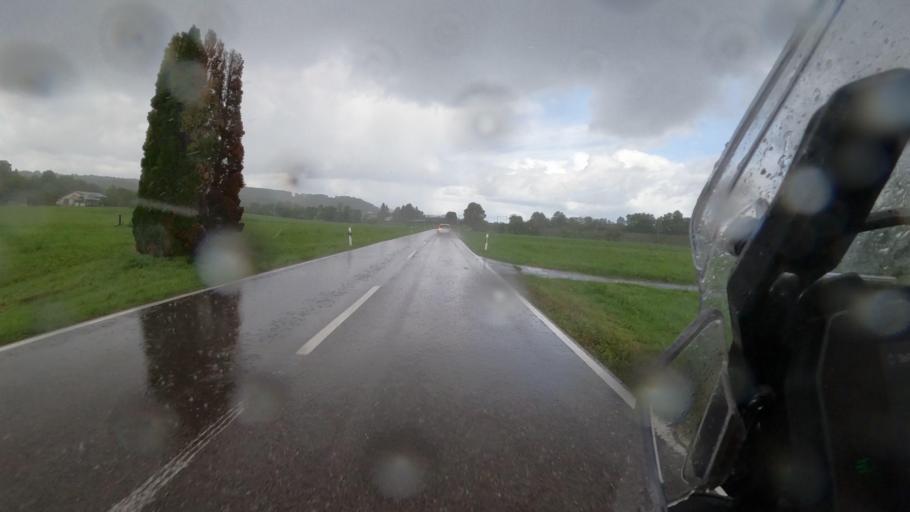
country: DE
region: Baden-Wuerttemberg
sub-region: Freiburg Region
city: Jestetten
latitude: 47.6444
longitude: 8.5591
